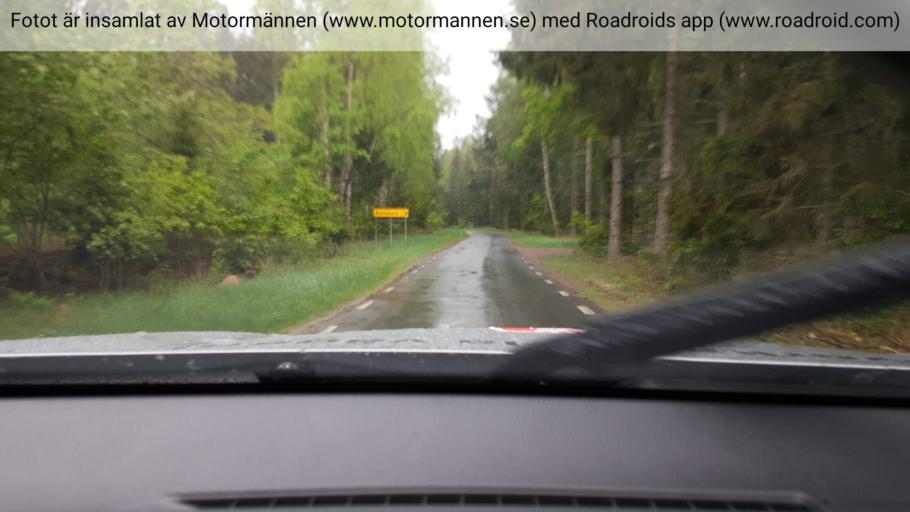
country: SE
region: Vaestra Goetaland
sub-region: Skara Kommun
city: Axvall
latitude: 58.3702
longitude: 13.5457
